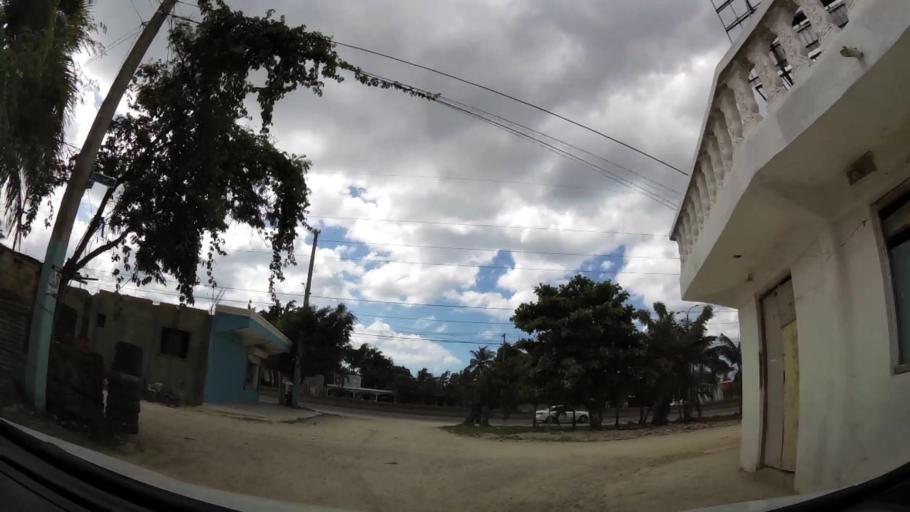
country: DO
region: Santo Domingo
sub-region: Santo Domingo
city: Boca Chica
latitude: 18.4485
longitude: -69.6444
